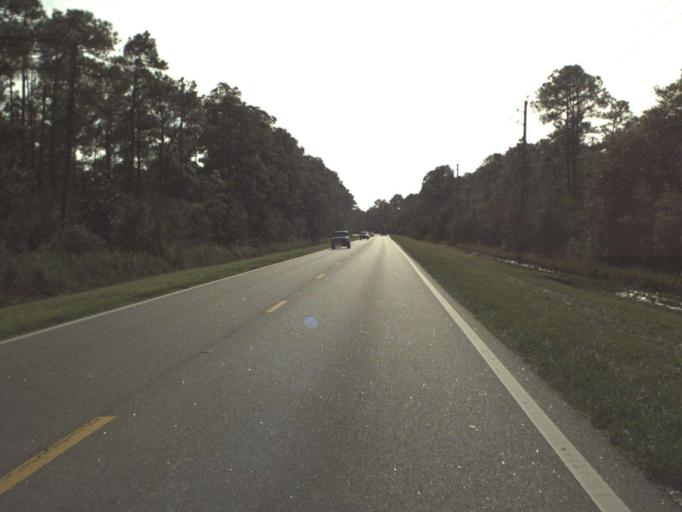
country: US
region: Florida
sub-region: Escambia County
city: Myrtle Grove
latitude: 30.3317
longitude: -87.4136
